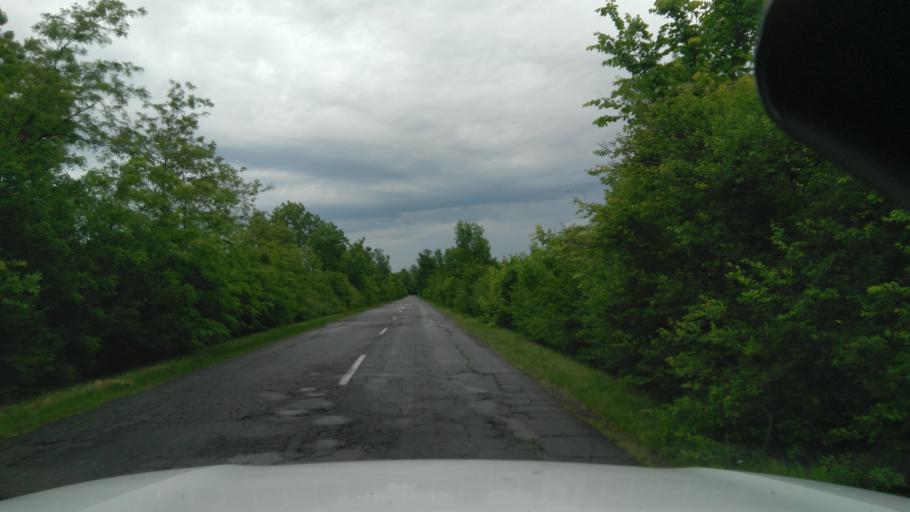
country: HU
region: Bekes
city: Bekescsaba
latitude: 46.6975
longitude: 21.1711
